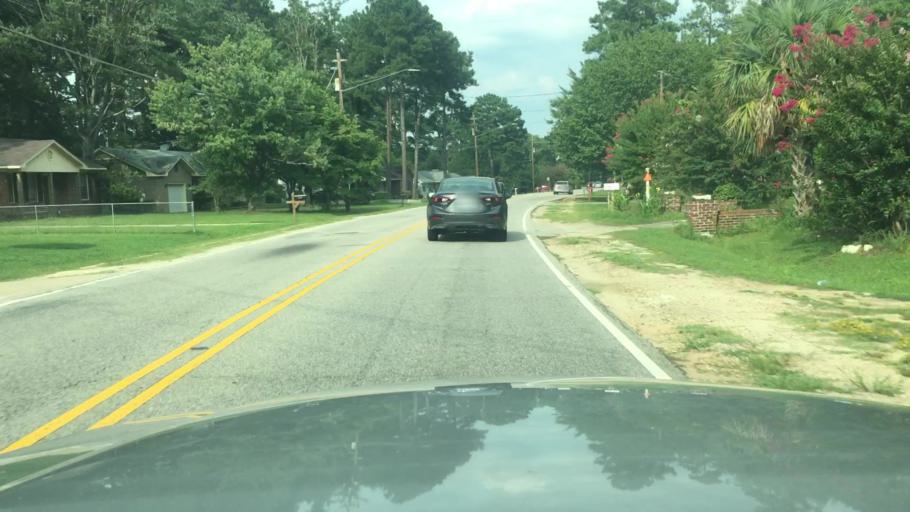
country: US
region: North Carolina
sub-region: Cumberland County
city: Fort Bragg
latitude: 35.1018
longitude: -79.0063
